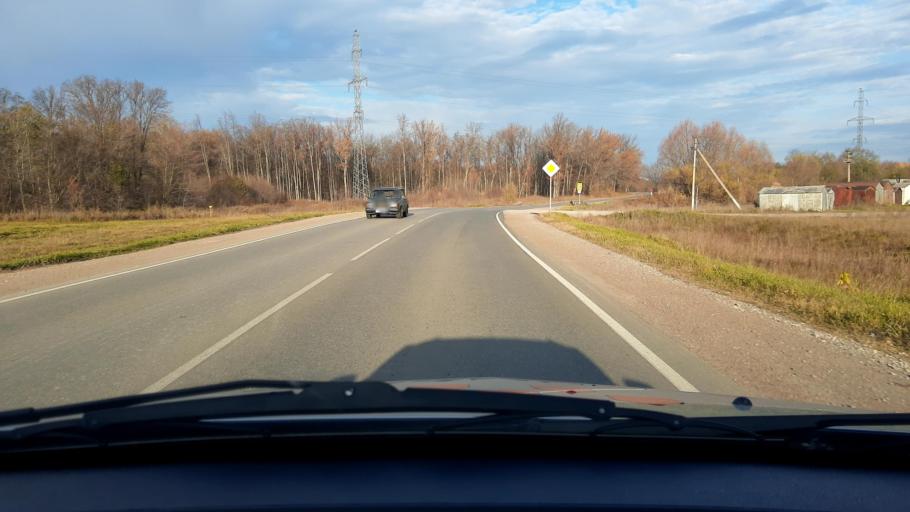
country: RU
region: Bashkortostan
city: Mikhaylovka
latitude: 54.8043
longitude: 55.8255
